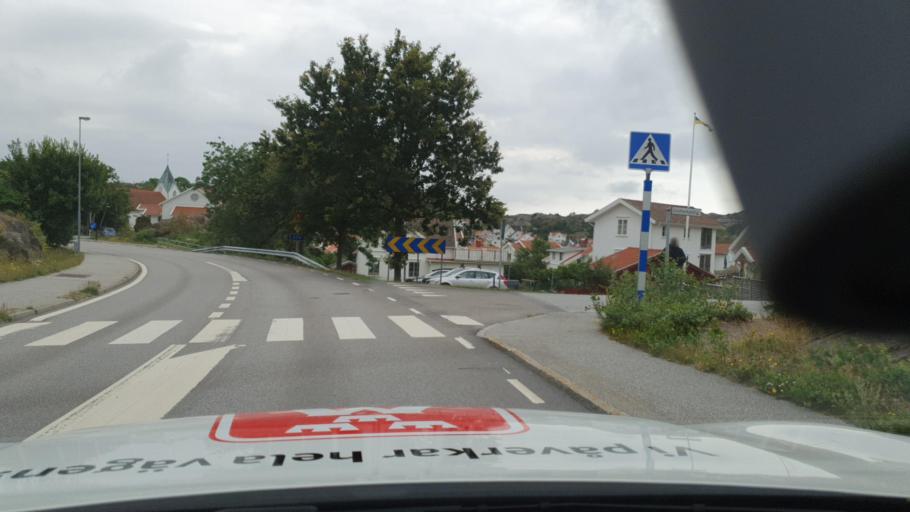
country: SE
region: Vaestra Goetaland
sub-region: Sotenas Kommun
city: Hunnebostrand
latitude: 58.4761
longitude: 11.3267
